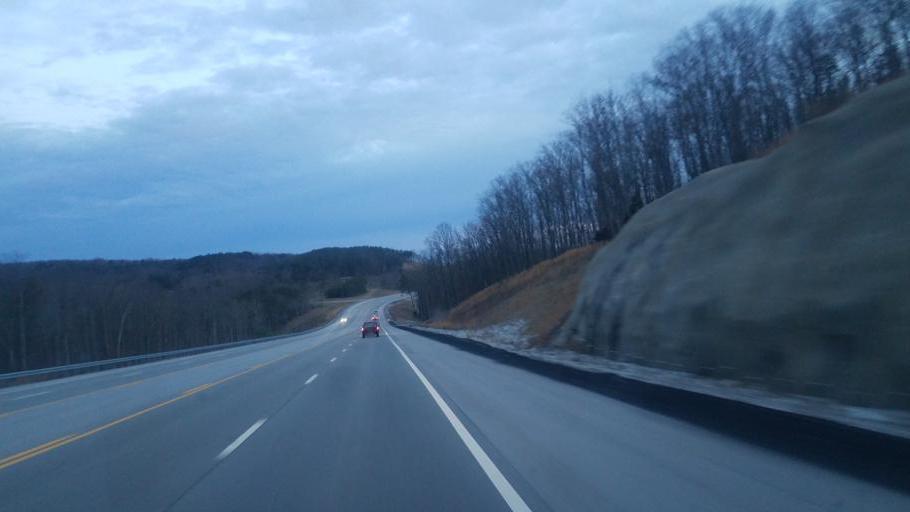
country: US
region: Tennessee
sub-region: Van Buren County
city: Spencer
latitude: 35.7645
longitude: -85.4617
